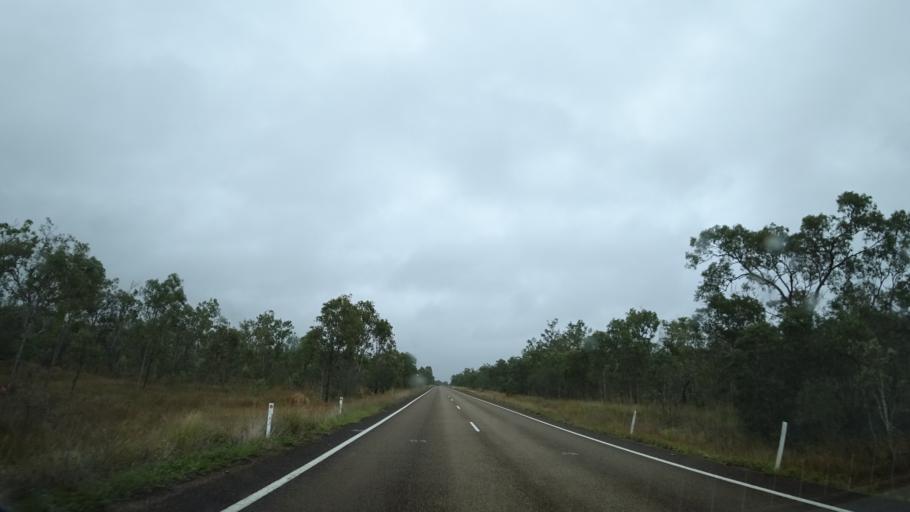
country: AU
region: Queensland
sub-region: Tablelands
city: Ravenshoe
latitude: -17.6886
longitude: 145.2264
